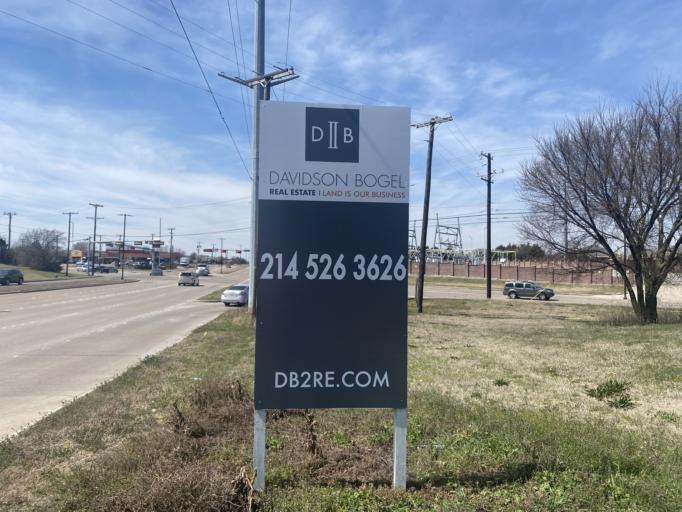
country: US
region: Texas
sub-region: Dallas County
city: Rowlett
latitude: 32.8946
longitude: -96.6009
